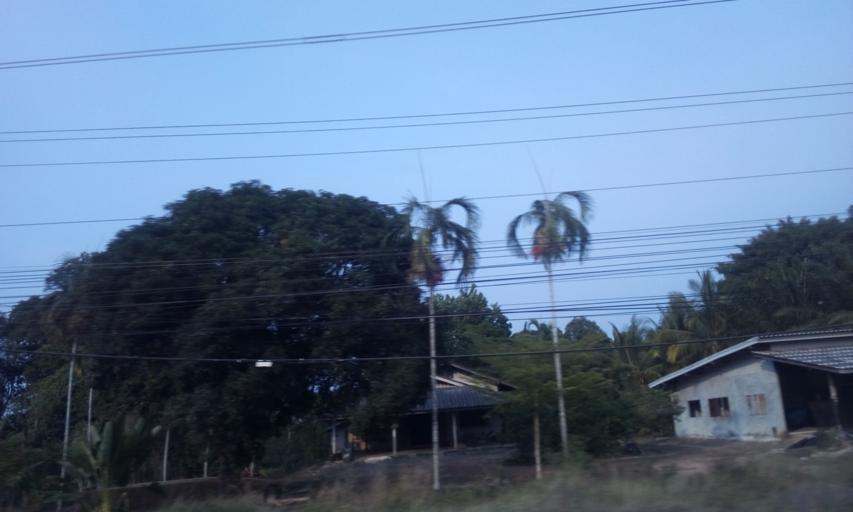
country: TH
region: Chanthaburi
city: Khlung
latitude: 12.4218
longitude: 102.3228
